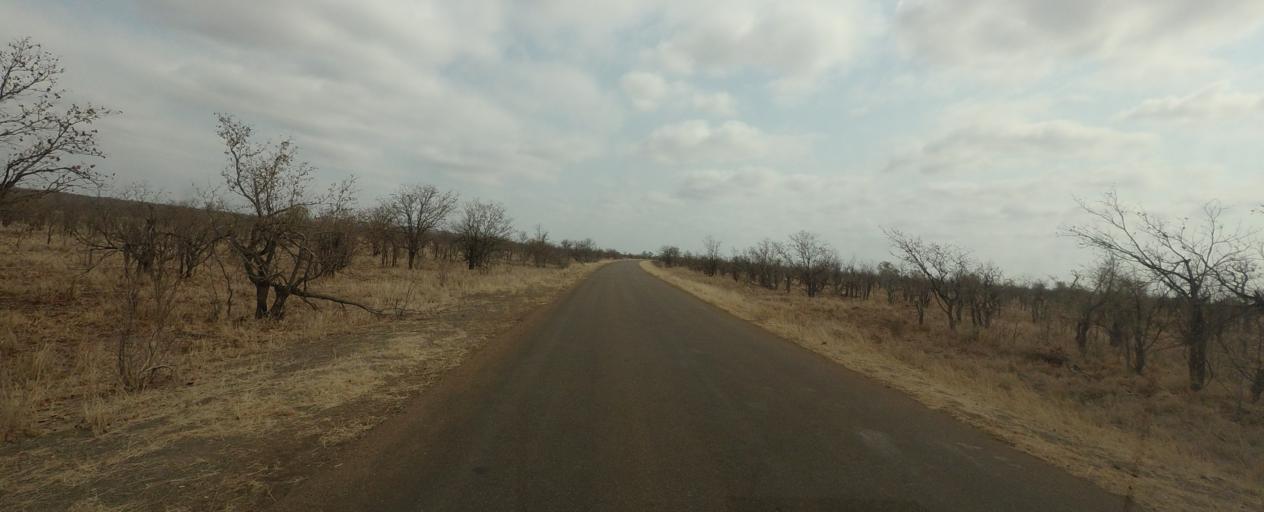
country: ZA
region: Limpopo
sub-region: Vhembe District Municipality
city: Mutale
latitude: -22.6165
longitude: 31.1744
